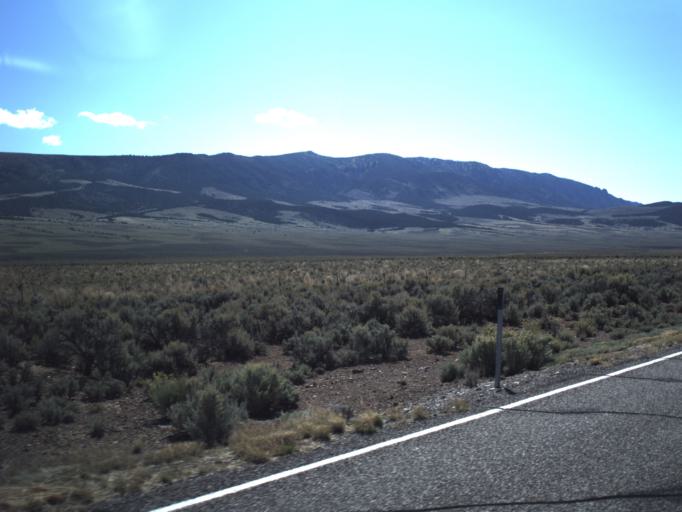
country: US
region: Utah
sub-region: Wayne County
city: Loa
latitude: 38.4142
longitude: -111.9253
